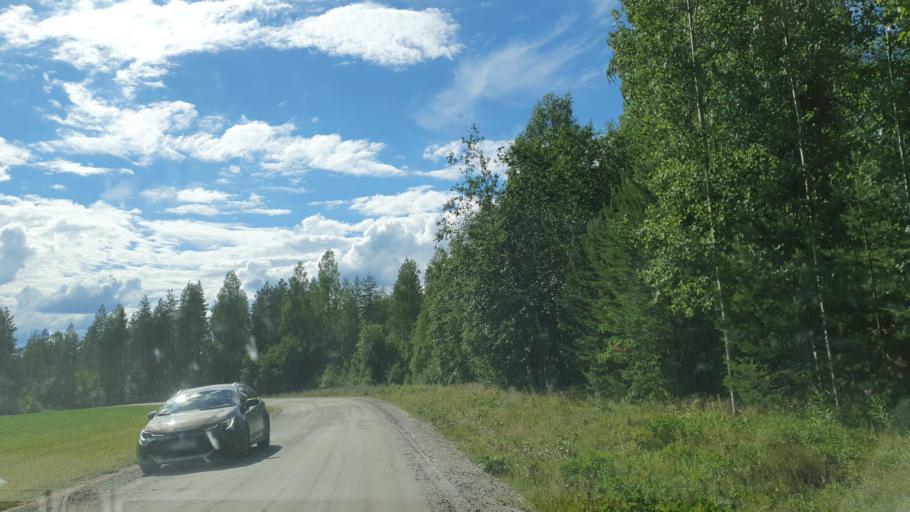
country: FI
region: Kainuu
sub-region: Kehys-Kainuu
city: Kuhmo
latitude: 64.1396
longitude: 29.6853
